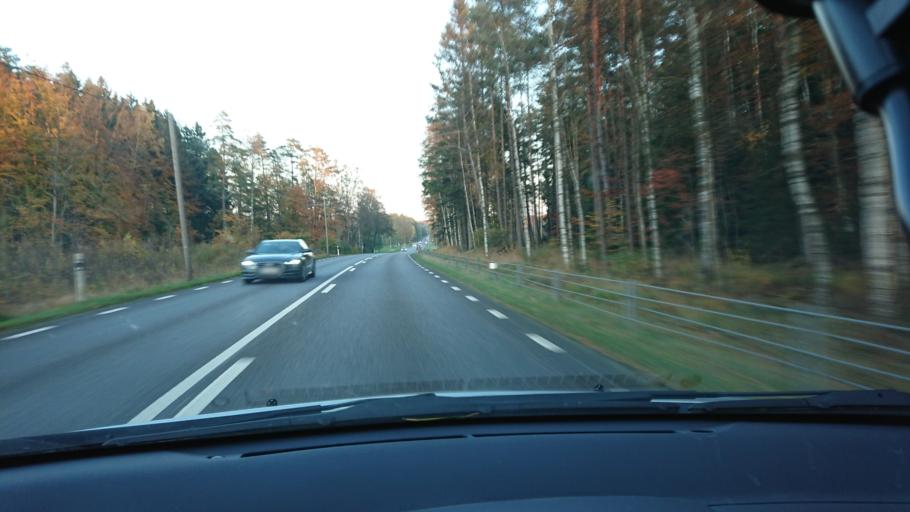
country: SE
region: Halland
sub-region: Halmstads Kommun
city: Oskarstrom
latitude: 56.7145
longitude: 13.1051
